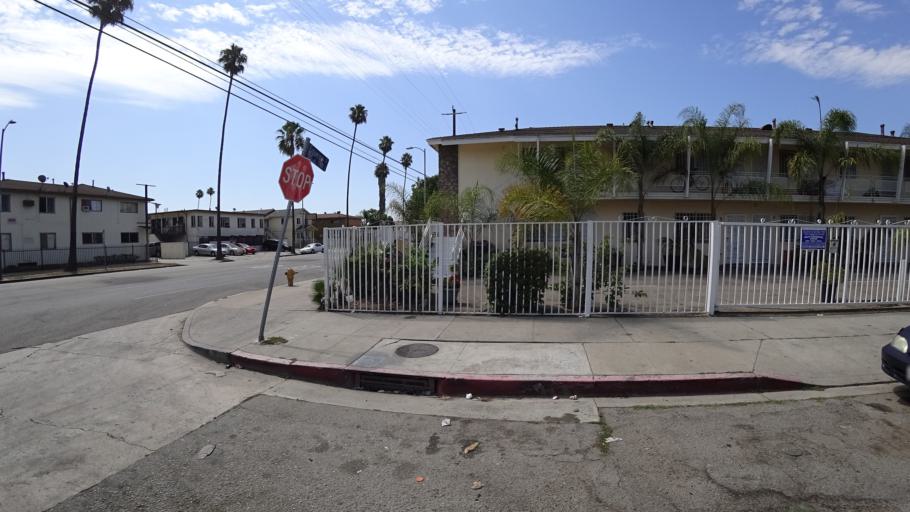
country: US
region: California
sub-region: Los Angeles County
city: Westmont
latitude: 33.9519
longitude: -118.2829
